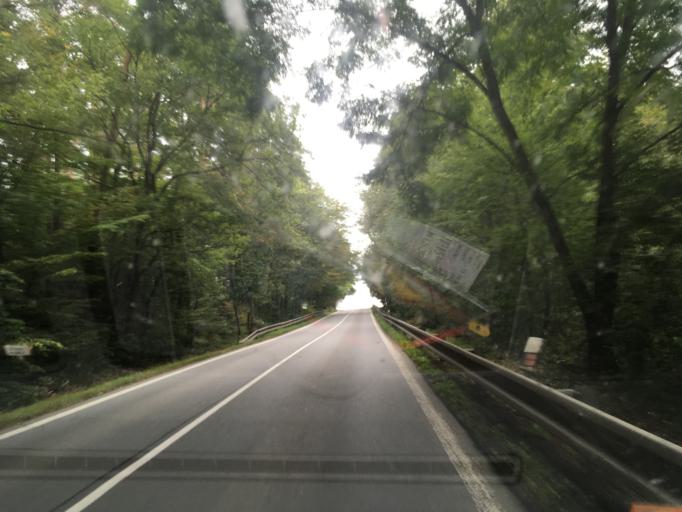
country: CZ
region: Vysocina
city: Namest' nad Oslavou
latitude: 49.1956
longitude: 16.2282
